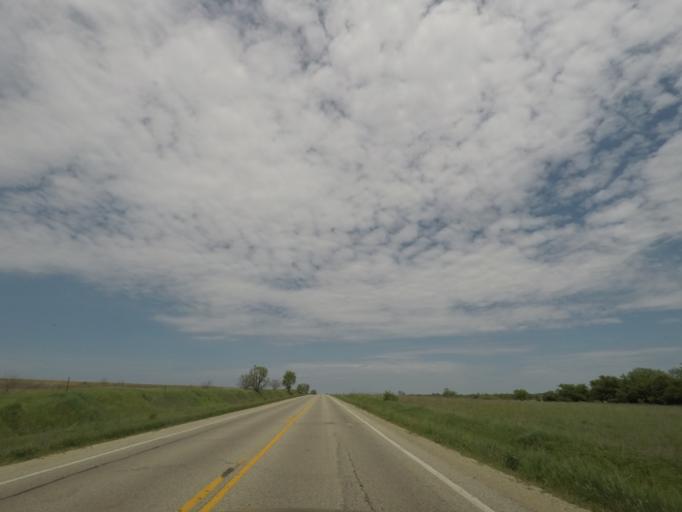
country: US
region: Wisconsin
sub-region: Rock County
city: Evansville
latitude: 42.7533
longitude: -89.2990
